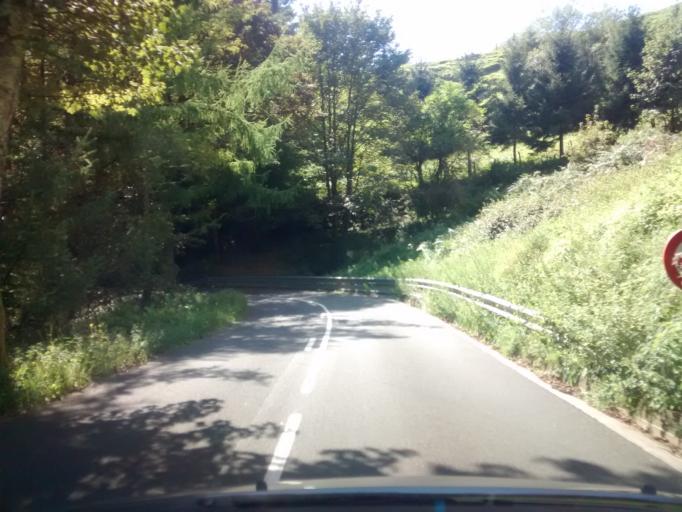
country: ES
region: Basque Country
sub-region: Provincia de Guipuzcoa
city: Eibar
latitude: 43.2103
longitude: -2.4679
